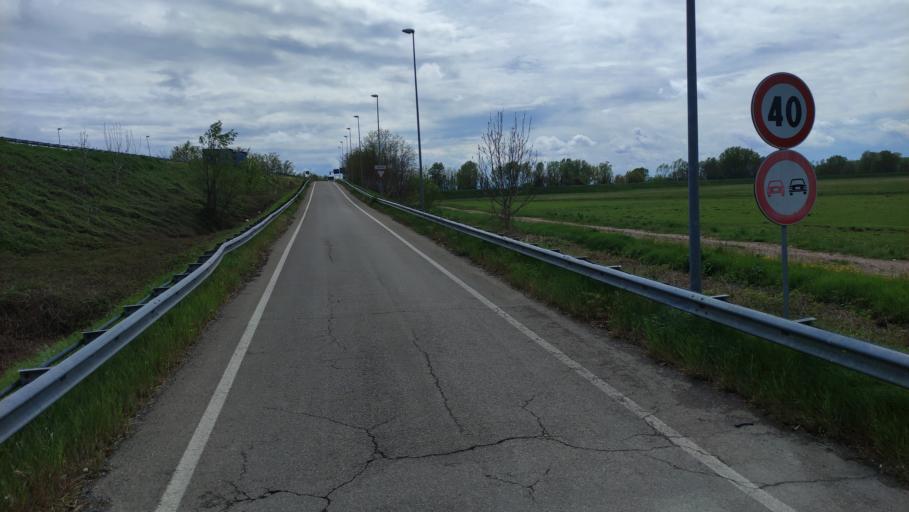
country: IT
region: Emilia-Romagna
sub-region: Provincia di Parma
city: Colorno
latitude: 44.9311
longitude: 10.3575
